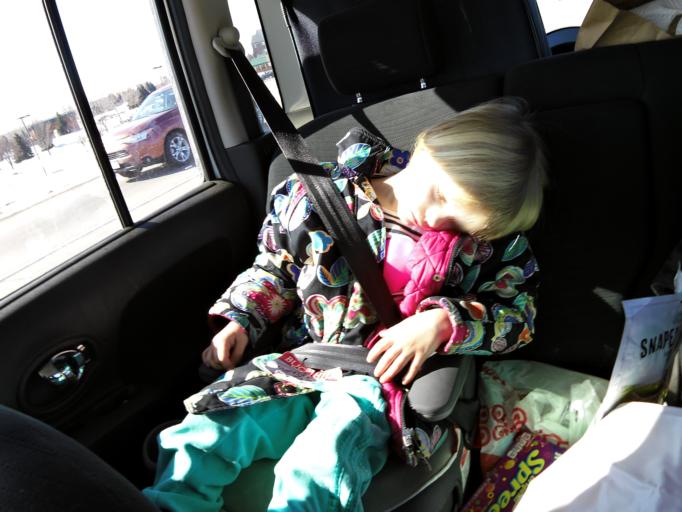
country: US
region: Minnesota
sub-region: Washington County
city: Lake Elmo
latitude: 44.9476
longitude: -92.9037
